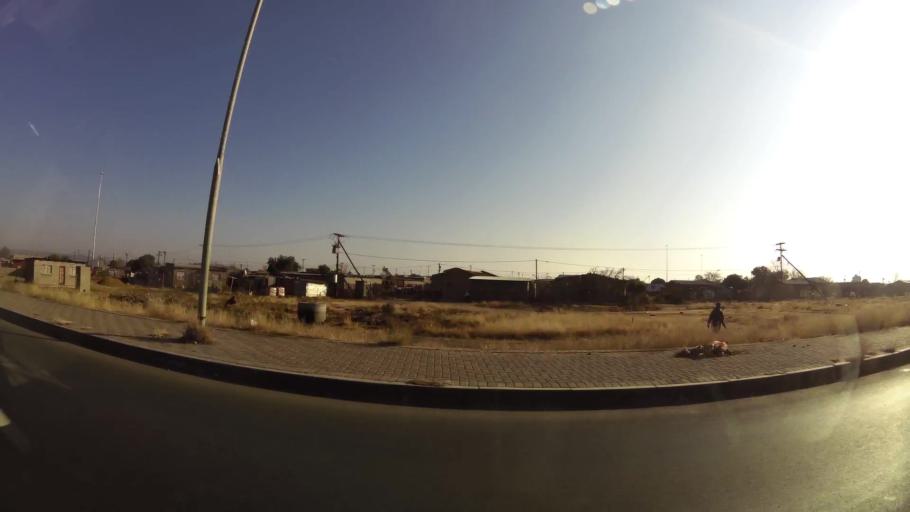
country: ZA
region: Orange Free State
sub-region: Mangaung Metropolitan Municipality
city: Bloemfontein
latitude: -29.1703
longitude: 26.2428
